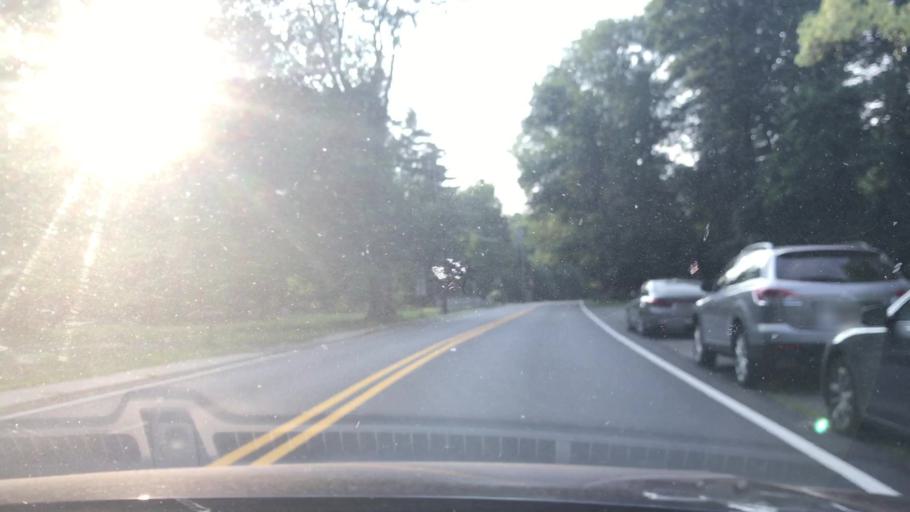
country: US
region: New Jersey
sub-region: Bergen County
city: Harrington Park
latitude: 40.9852
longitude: -73.9937
